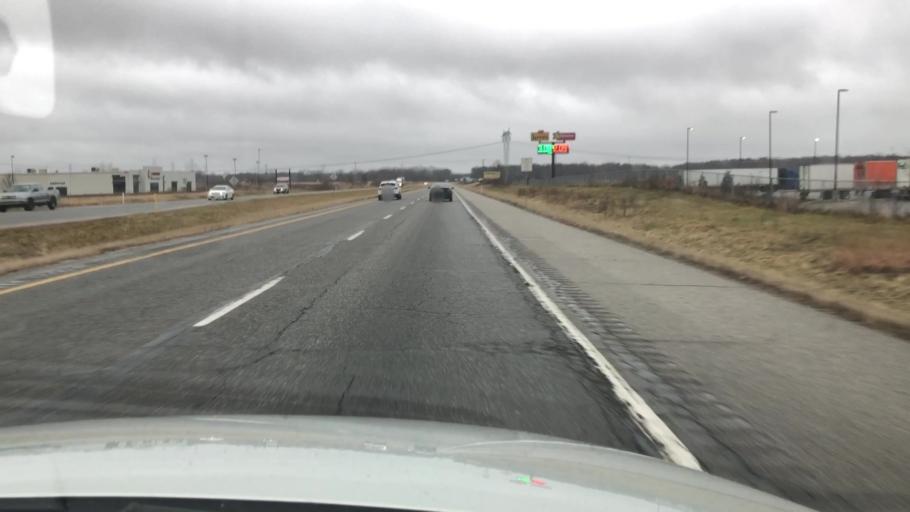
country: US
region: Indiana
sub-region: Marshall County
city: Plymouth
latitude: 41.3615
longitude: -86.3502
